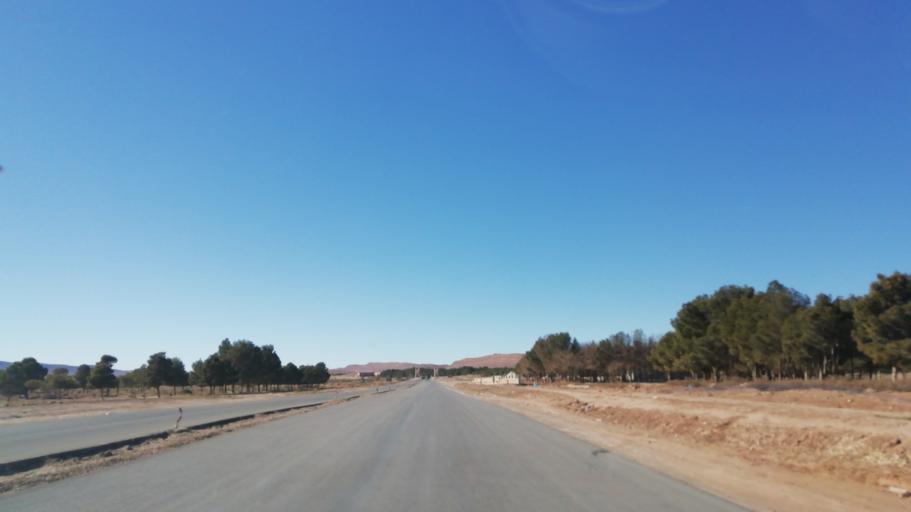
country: DZ
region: El Bayadh
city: El Bayadh
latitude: 33.7242
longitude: 1.5259
